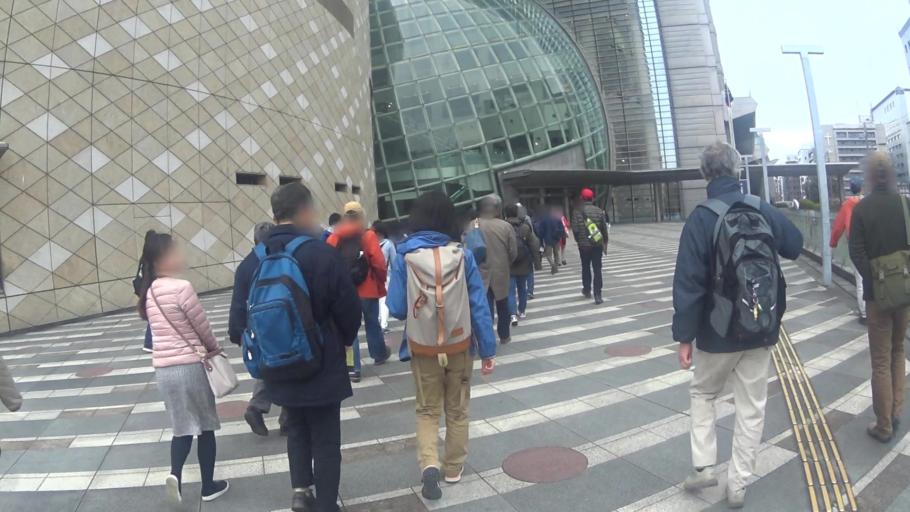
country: JP
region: Osaka
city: Osaka-shi
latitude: 34.6827
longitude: 135.5208
